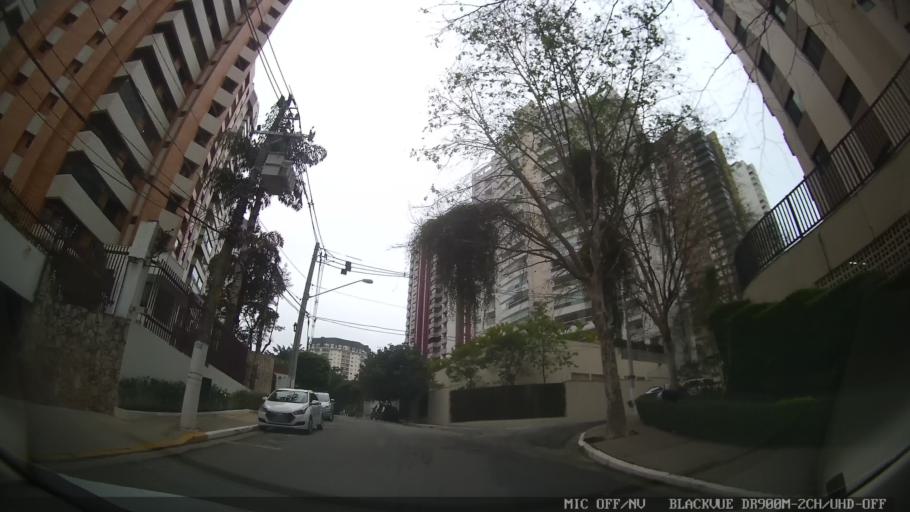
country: BR
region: Sao Paulo
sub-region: Sao Paulo
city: Sao Paulo
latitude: -23.5908
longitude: -46.6226
